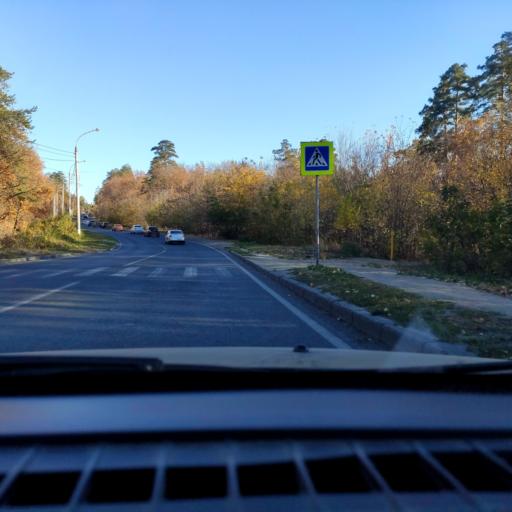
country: RU
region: Samara
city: Tol'yatti
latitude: 53.4942
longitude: 49.2916
